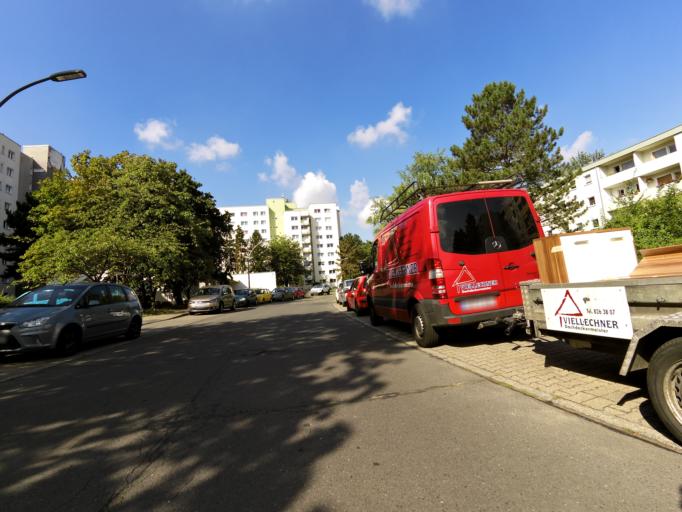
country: DE
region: Berlin
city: Lichtenrade
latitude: 52.3891
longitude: 13.4158
